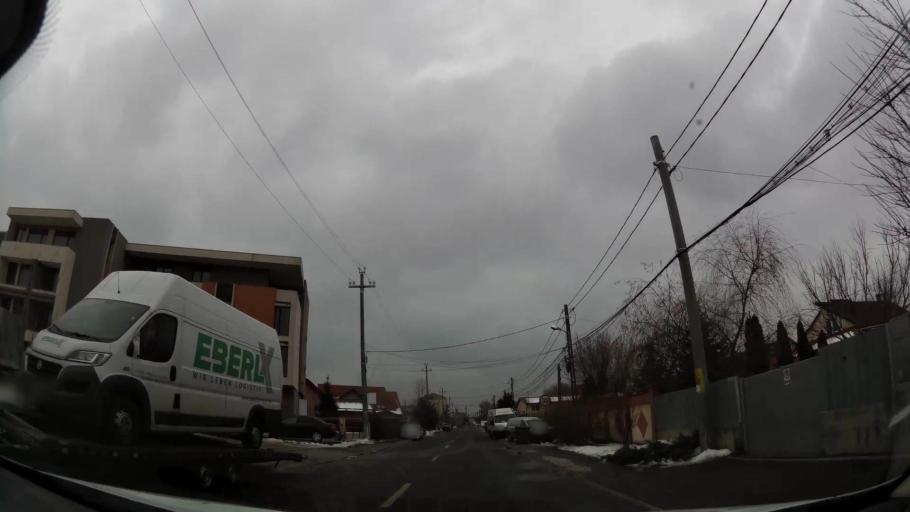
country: RO
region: Ilfov
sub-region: Comuna Otopeni
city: Otopeni
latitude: 44.5545
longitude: 26.0800
